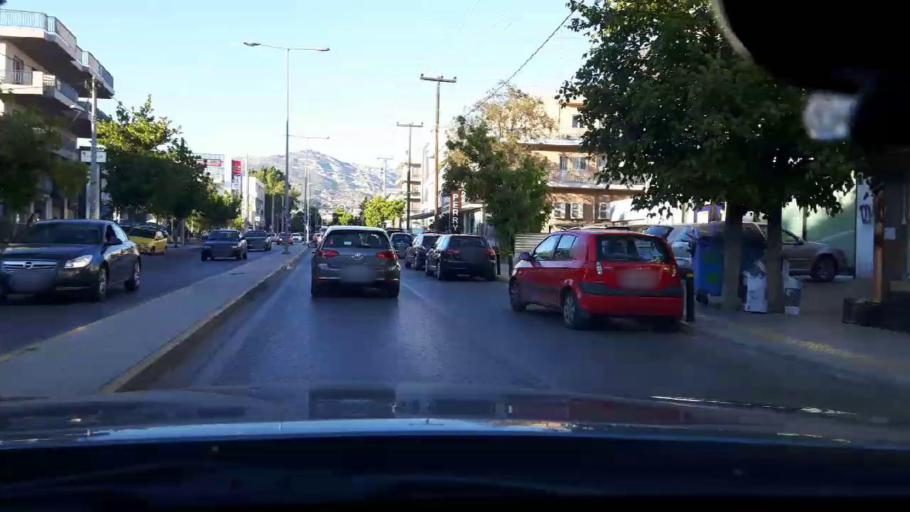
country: GR
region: Attica
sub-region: Nomarchia Athinas
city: Vrilissia
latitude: 38.0389
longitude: 23.8291
